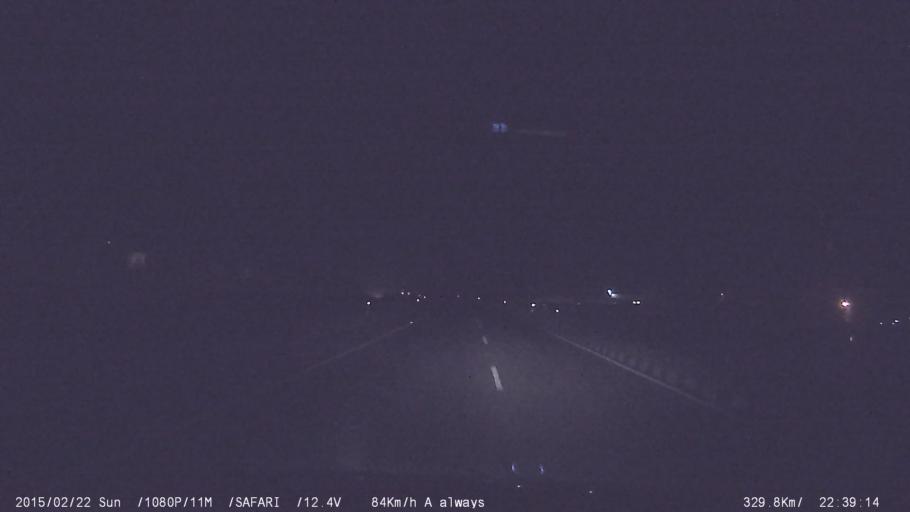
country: IN
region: Tamil Nadu
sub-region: Namakkal
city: Velur
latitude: 11.1713
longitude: 78.0434
